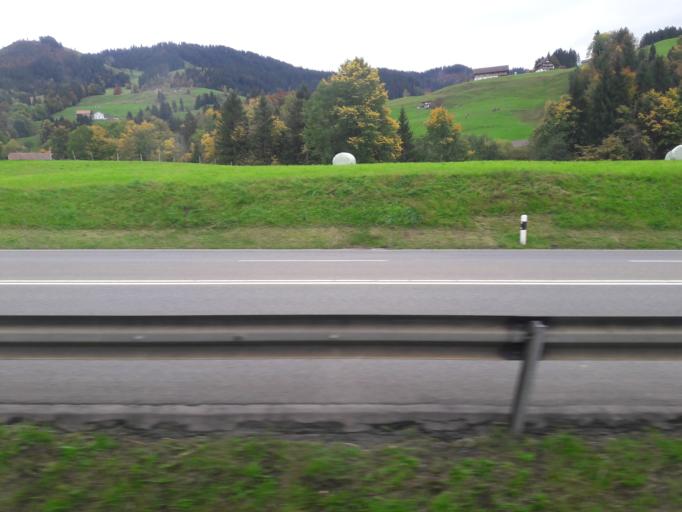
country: CH
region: Schwyz
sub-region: Bezirk Schwyz
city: Rothenthurm
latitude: 47.0910
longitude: 8.6673
